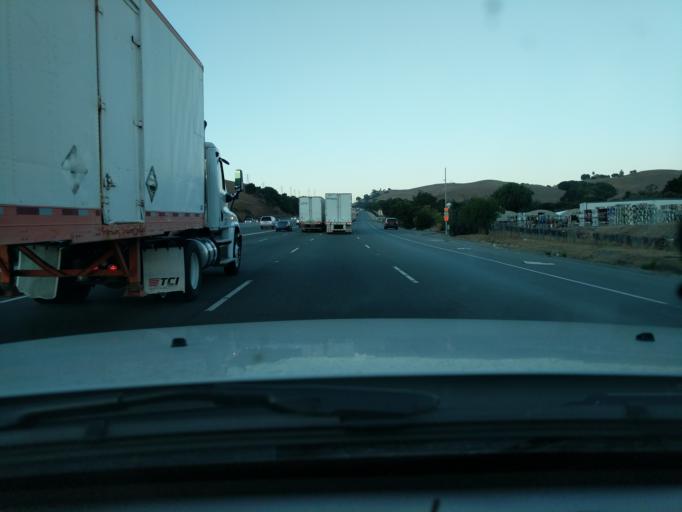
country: US
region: California
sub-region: Alameda County
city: Pleasanton
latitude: 37.5716
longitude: -121.8900
